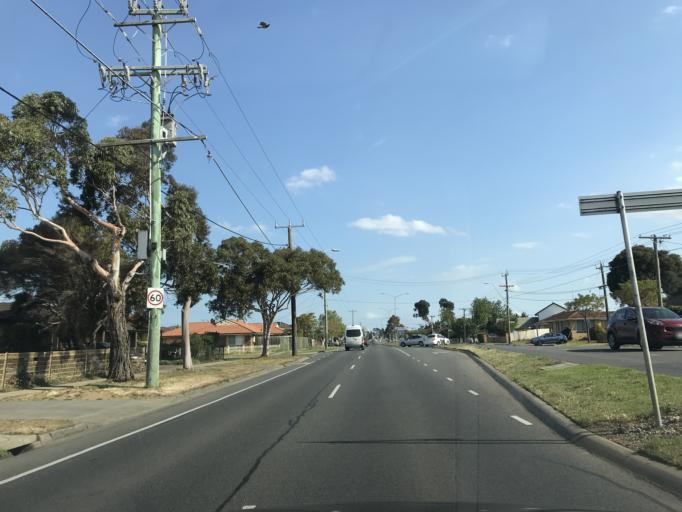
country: AU
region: Victoria
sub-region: Wyndham
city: Hoppers Crossing
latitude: -37.8747
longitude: 144.7022
